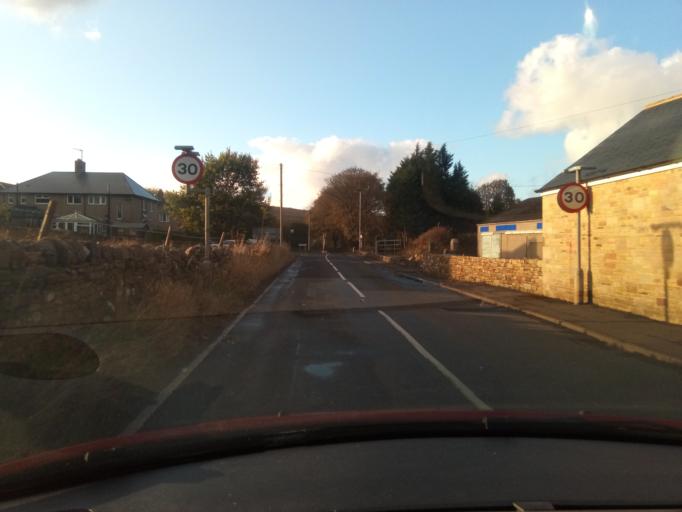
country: GB
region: England
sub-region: County Durham
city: Holwick
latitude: 54.7486
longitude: -2.2192
